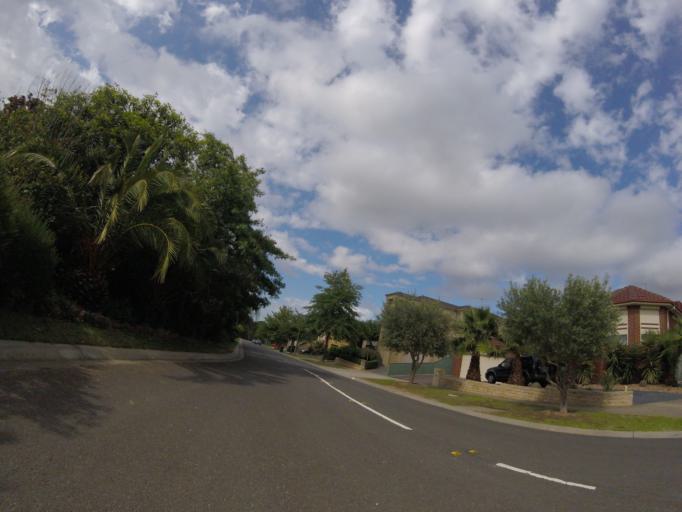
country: AU
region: Victoria
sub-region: Hume
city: Attwood
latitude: -37.6692
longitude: 144.8948
